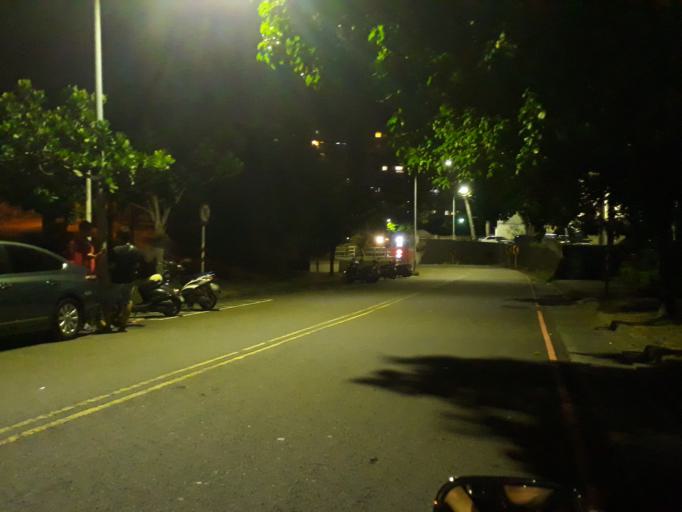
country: TW
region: Taiwan
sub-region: Hsinchu
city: Hsinchu
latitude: 24.7988
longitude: 120.9954
